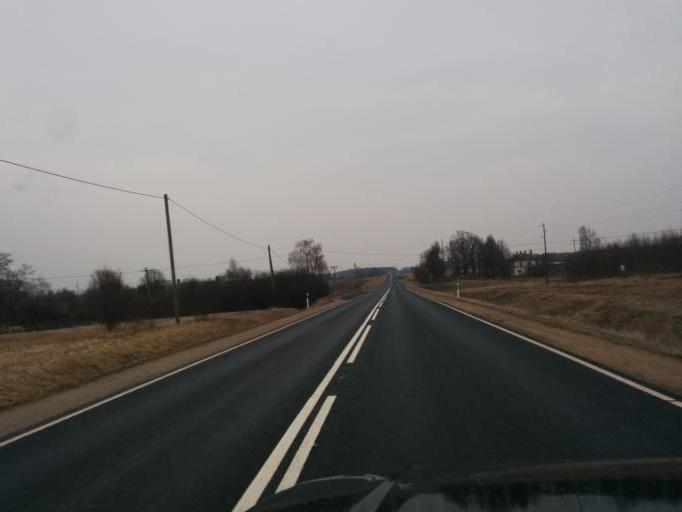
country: LV
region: Salaspils
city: Salaspils
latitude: 56.8266
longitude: 24.3429
